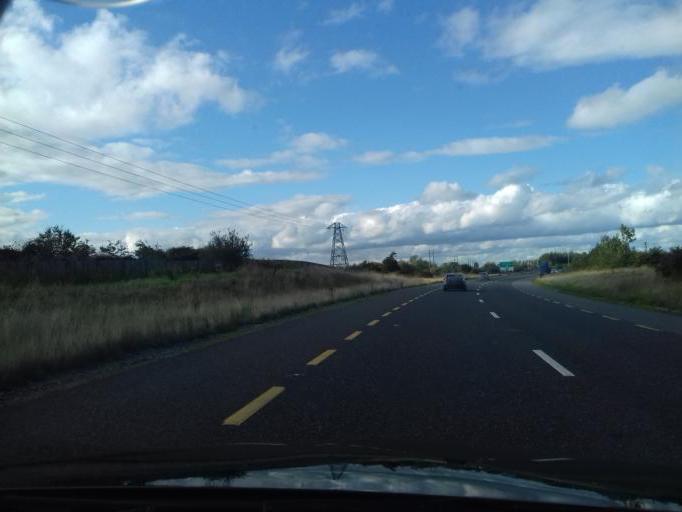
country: IE
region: Leinster
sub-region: Uibh Fhaili
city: Tullamore
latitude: 53.2735
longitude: -7.4663
